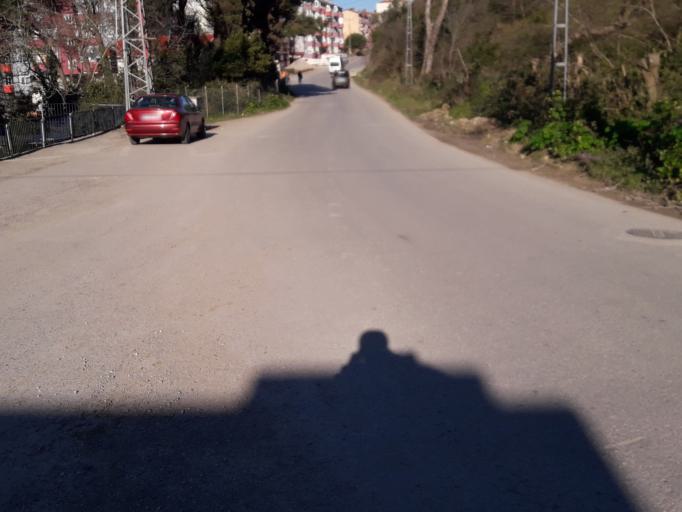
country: TR
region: Sinop
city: Sinop
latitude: 42.0219
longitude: 35.1255
